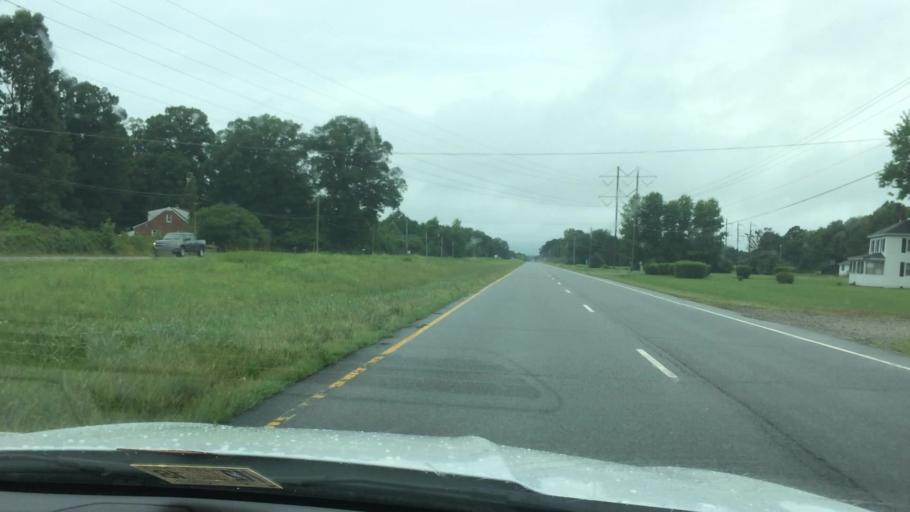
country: US
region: Virginia
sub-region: King William County
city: West Point
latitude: 37.5447
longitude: -76.7456
